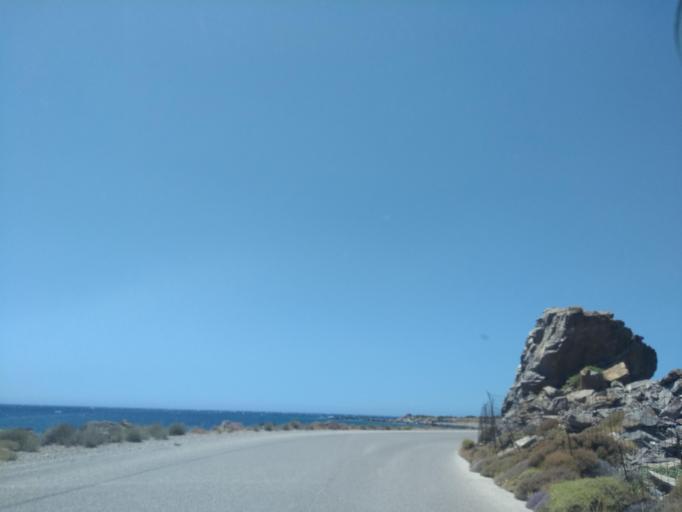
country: GR
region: Crete
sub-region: Nomos Chanias
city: Vryses
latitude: 35.3508
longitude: 23.5371
